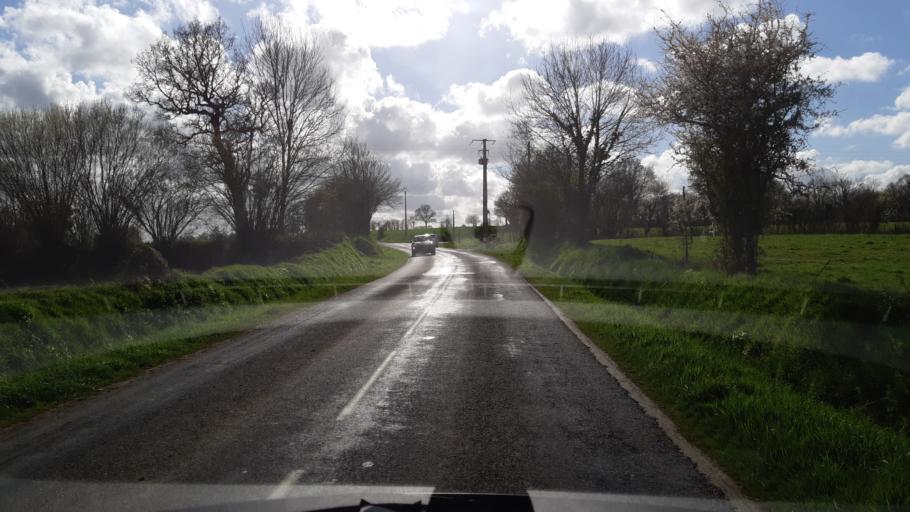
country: FR
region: Lower Normandy
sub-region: Departement de la Manche
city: Agneaux
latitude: 49.0253
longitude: -1.1540
